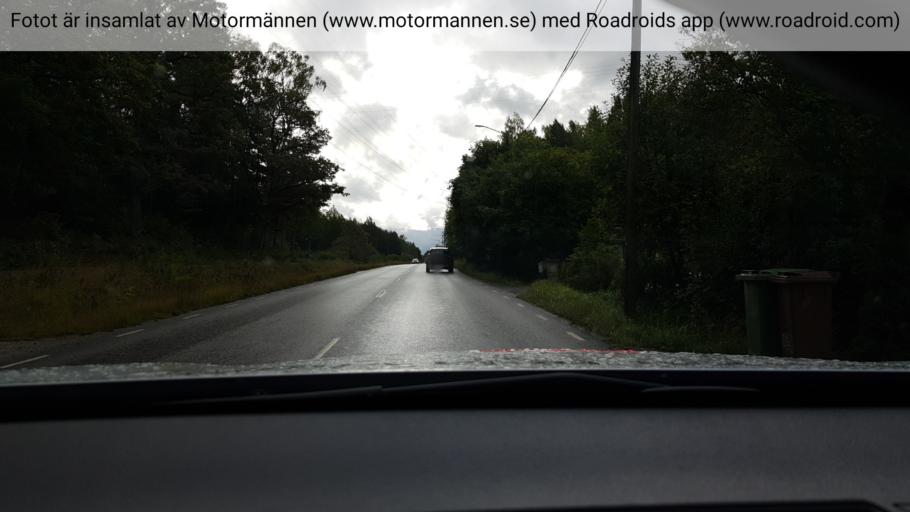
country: SE
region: Stockholm
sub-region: Huddinge Kommun
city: Huddinge
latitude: 59.2337
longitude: 18.0402
